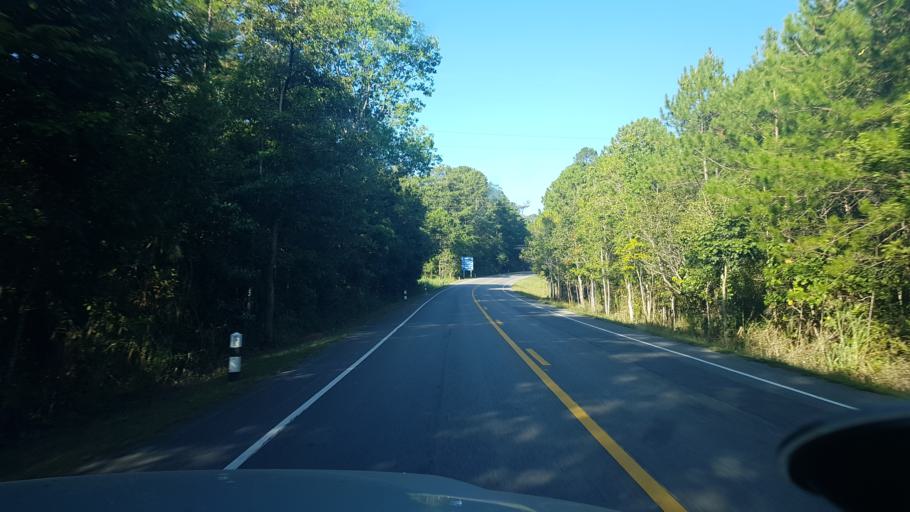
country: TH
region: Phetchabun
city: Nam Nao
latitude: 16.7301
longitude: 101.5576
